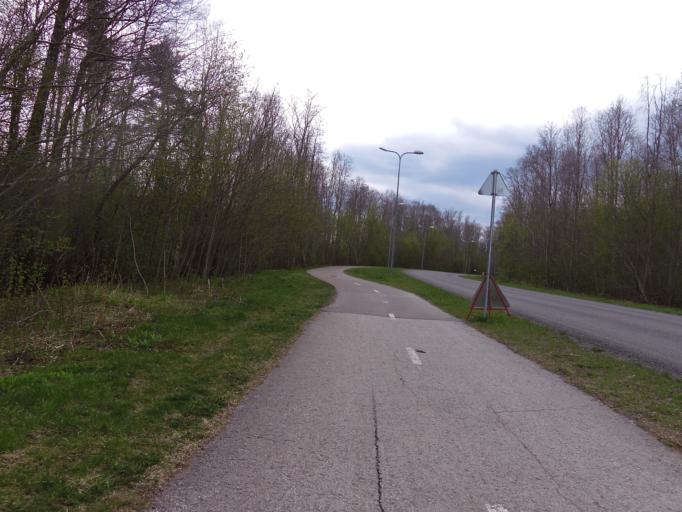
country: EE
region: Harju
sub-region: Kiili vald
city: Kiili
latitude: 59.3641
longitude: 24.8163
